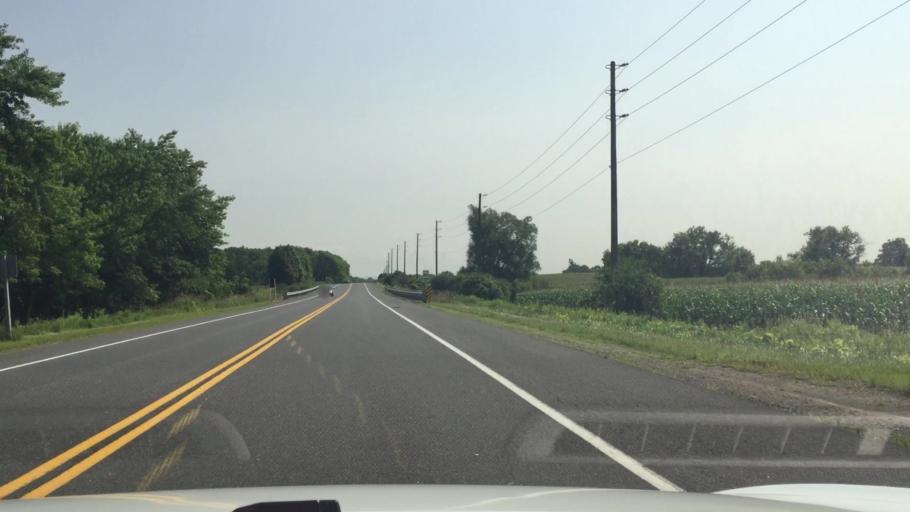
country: CA
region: Ontario
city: Pickering
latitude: 43.9122
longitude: -79.1357
